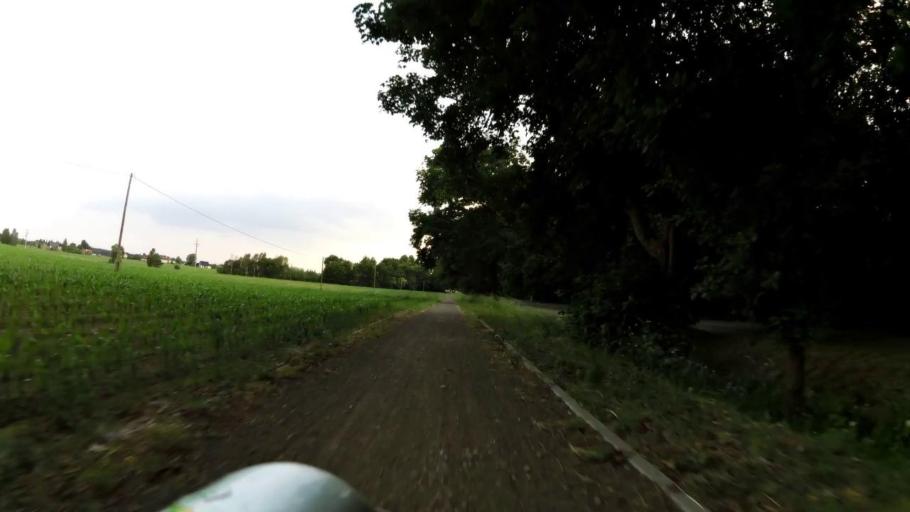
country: PL
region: Kujawsko-Pomorskie
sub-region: Powiat bydgoski
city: Dabrowa Chelminska
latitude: 53.1836
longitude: 18.3354
